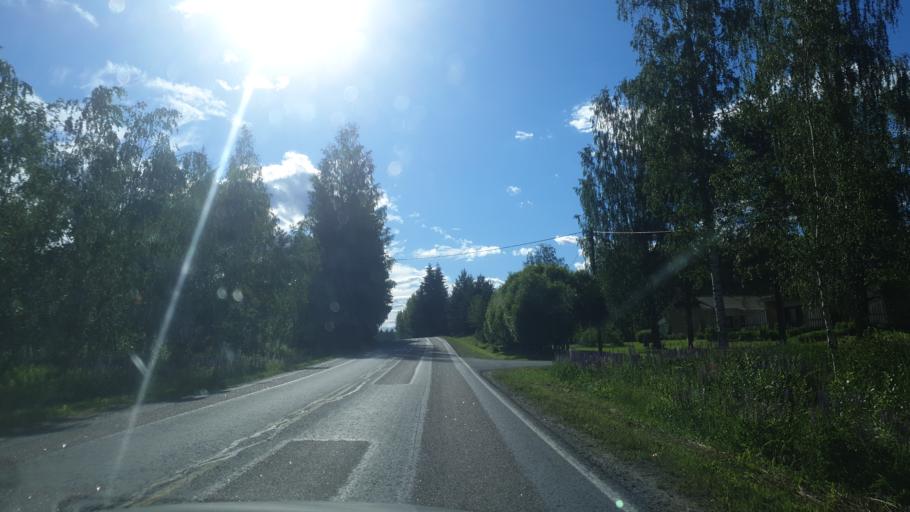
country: FI
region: Southern Savonia
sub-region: Mikkeli
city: Pertunmaa
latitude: 61.5244
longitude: 26.5389
